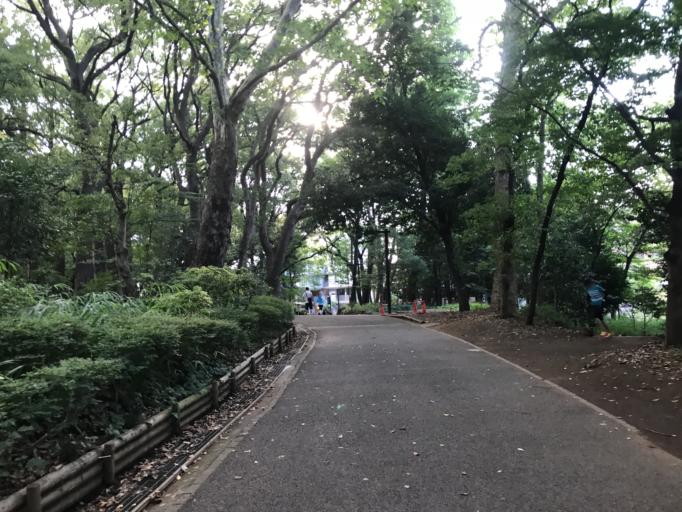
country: JP
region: Tokyo
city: Tokyo
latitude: 35.6257
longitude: 139.7013
